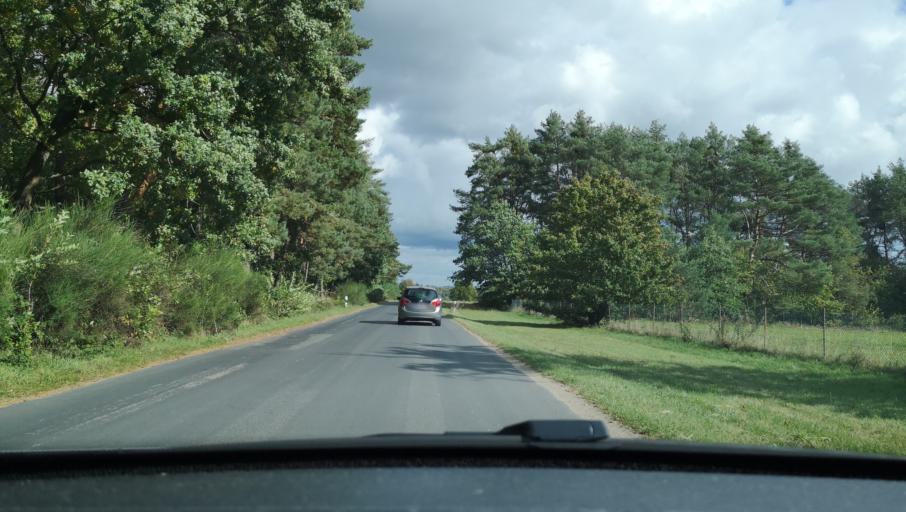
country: DE
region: Hesse
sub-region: Regierungsbezirk Darmstadt
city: Rodgau
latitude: 50.0145
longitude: 8.9162
